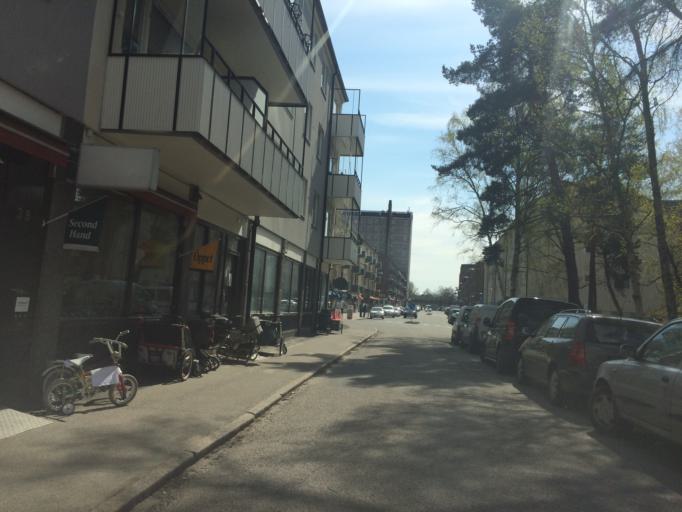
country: SE
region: Stockholm
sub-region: Huddinge Kommun
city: Segeltorp
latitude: 59.2946
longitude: 17.9661
